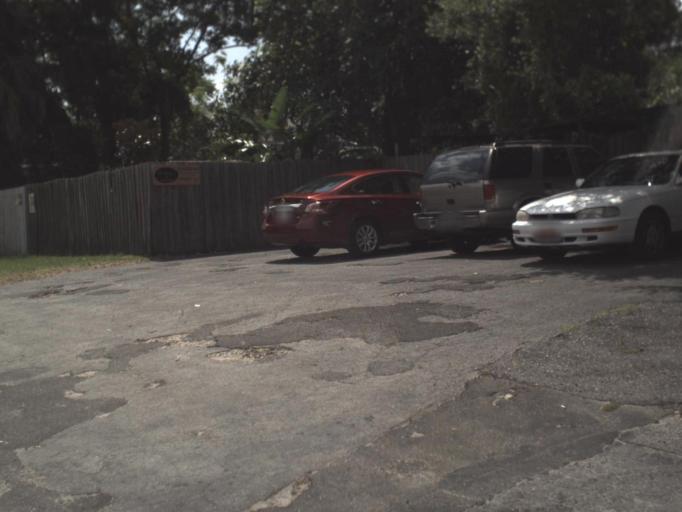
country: US
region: Florida
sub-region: Pinellas County
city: Saint Petersburg
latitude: 27.7773
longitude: -82.6668
